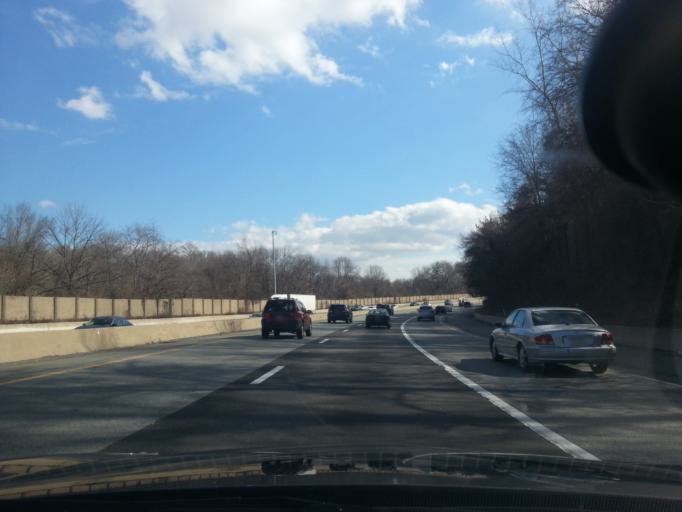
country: US
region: Pennsylvania
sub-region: Delaware County
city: Broomall
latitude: 39.9849
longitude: -75.3392
